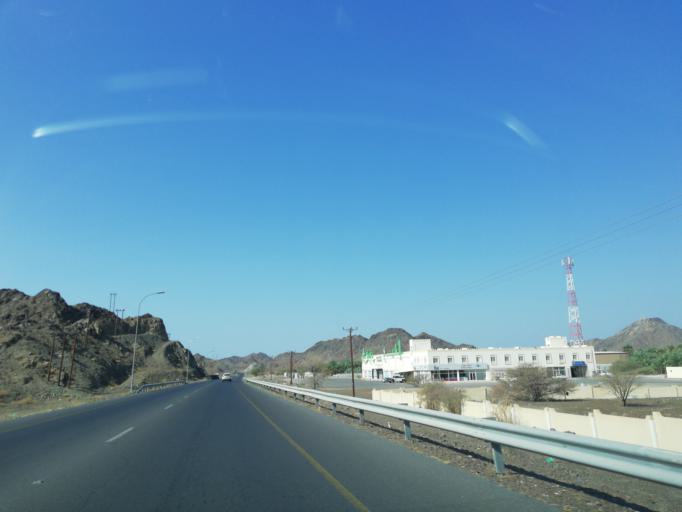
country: OM
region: Ash Sharqiyah
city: Ibra'
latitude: 22.8281
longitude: 58.1701
